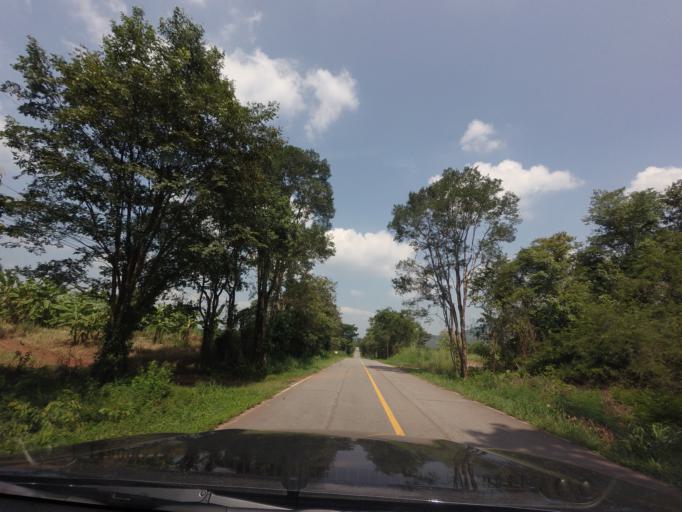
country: TH
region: Uttaradit
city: Ban Khok
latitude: 17.9170
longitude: 100.9892
